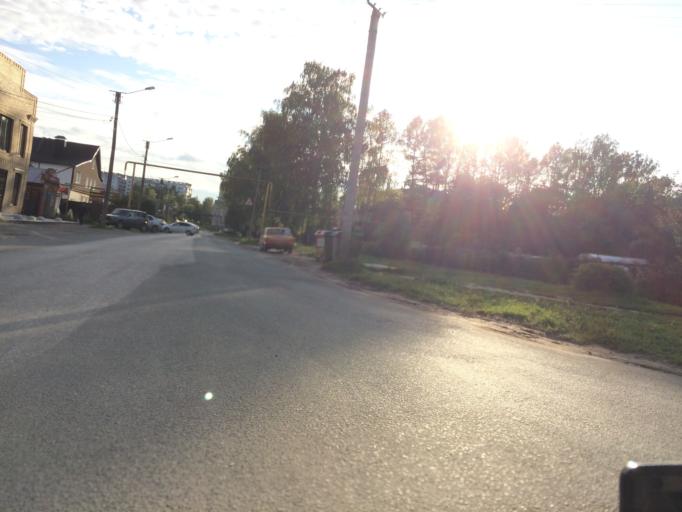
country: RU
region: Mariy-El
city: Yoshkar-Ola
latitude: 56.6532
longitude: 47.9781
